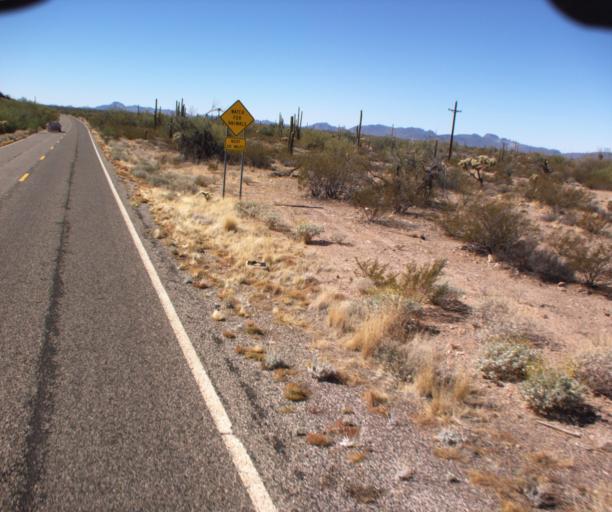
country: US
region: Arizona
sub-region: Pima County
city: Ajo
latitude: 32.2283
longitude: -112.7545
